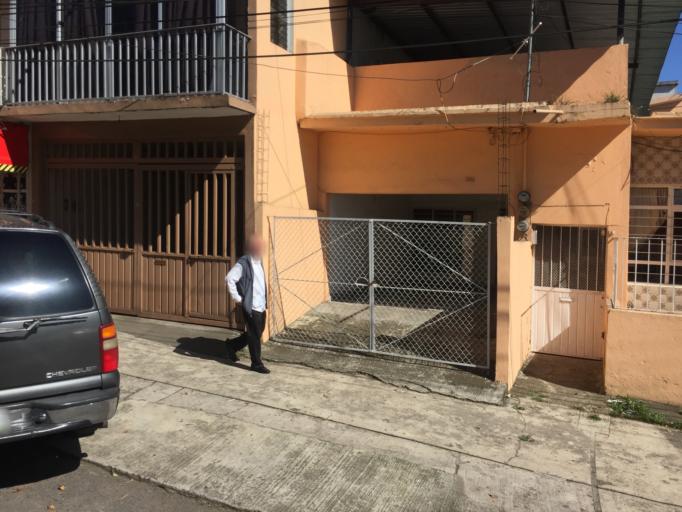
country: MX
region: Veracruz
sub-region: Xalapa
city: Xalapa de Enriquez
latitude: 19.5501
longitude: -96.9297
